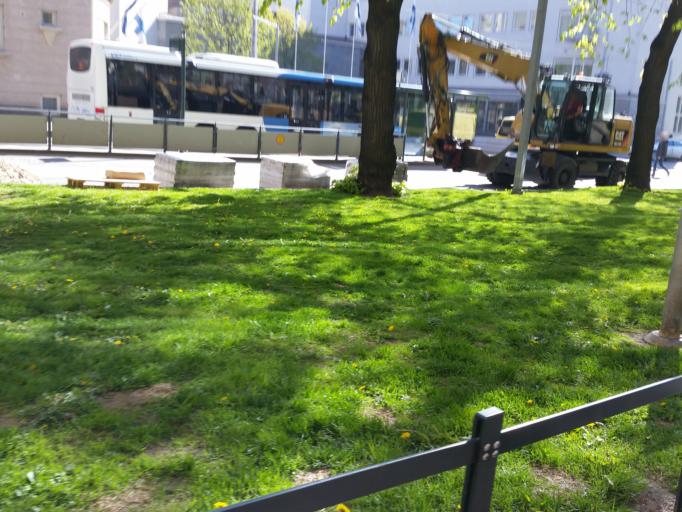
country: FI
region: Uusimaa
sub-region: Helsinki
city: Helsinki
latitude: 60.1714
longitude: 24.9254
